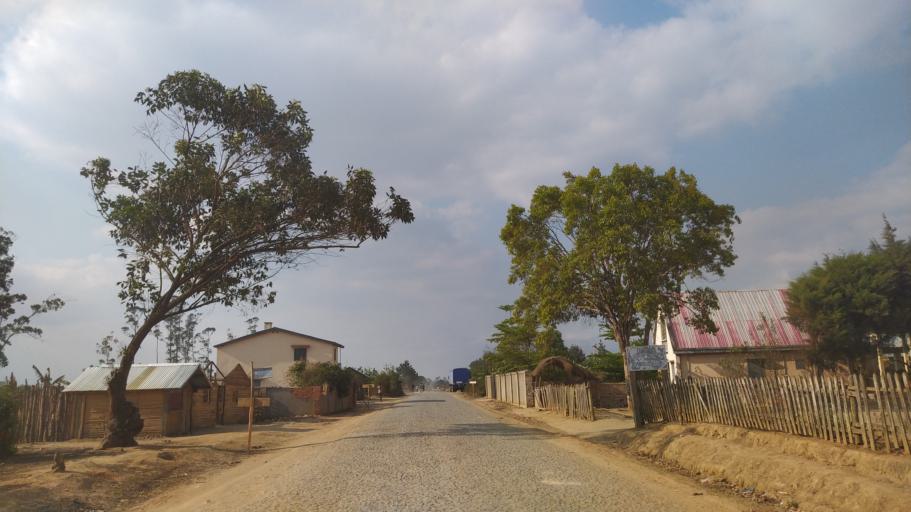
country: MG
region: Alaotra Mangoro
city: Moramanga
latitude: -18.6358
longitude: 48.2758
